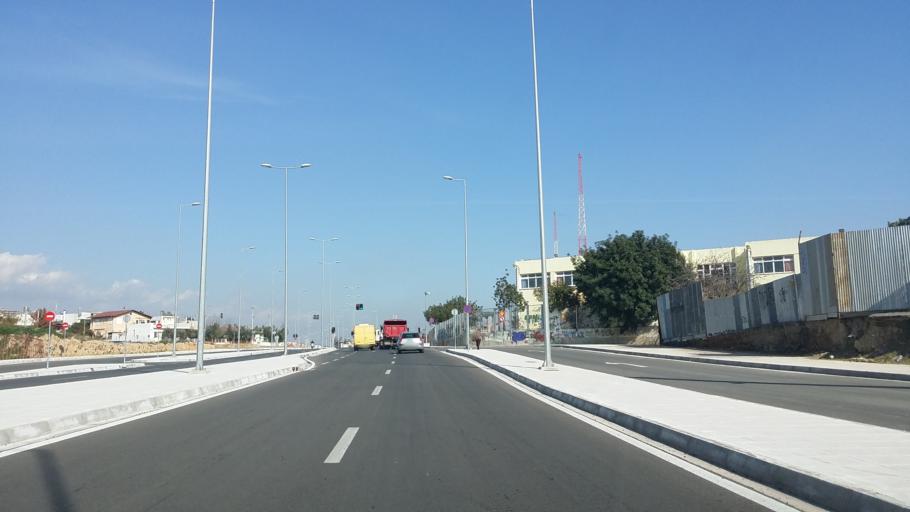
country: GR
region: Attica
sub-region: Nomarchia Athinas
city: Ilion
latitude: 38.0385
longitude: 23.7060
